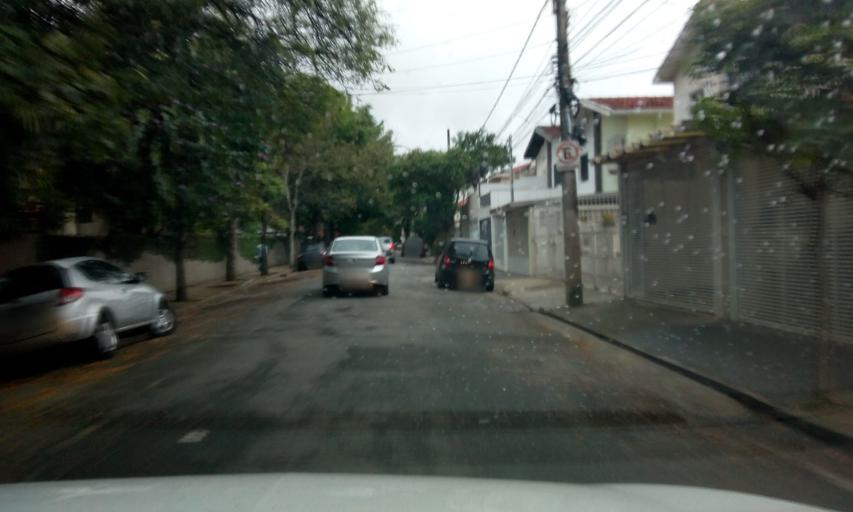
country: BR
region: Sao Paulo
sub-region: Sao Paulo
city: Sao Paulo
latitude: -23.6052
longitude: -46.6886
